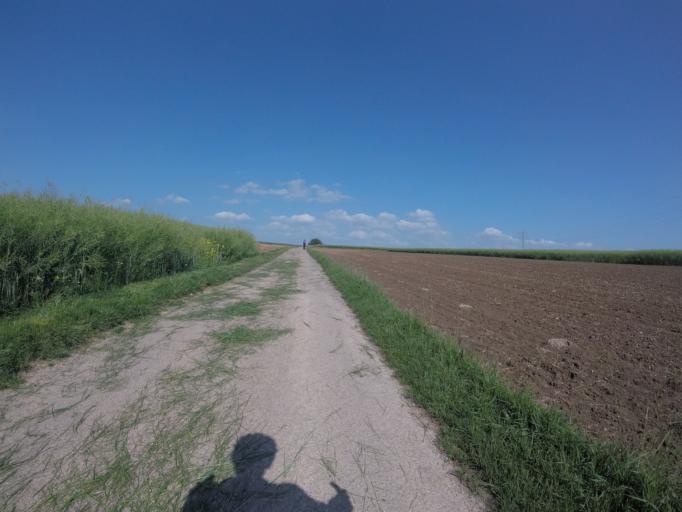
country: DE
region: Baden-Wuerttemberg
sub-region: Regierungsbezirk Stuttgart
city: Aspach
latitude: 48.9609
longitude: 9.3791
